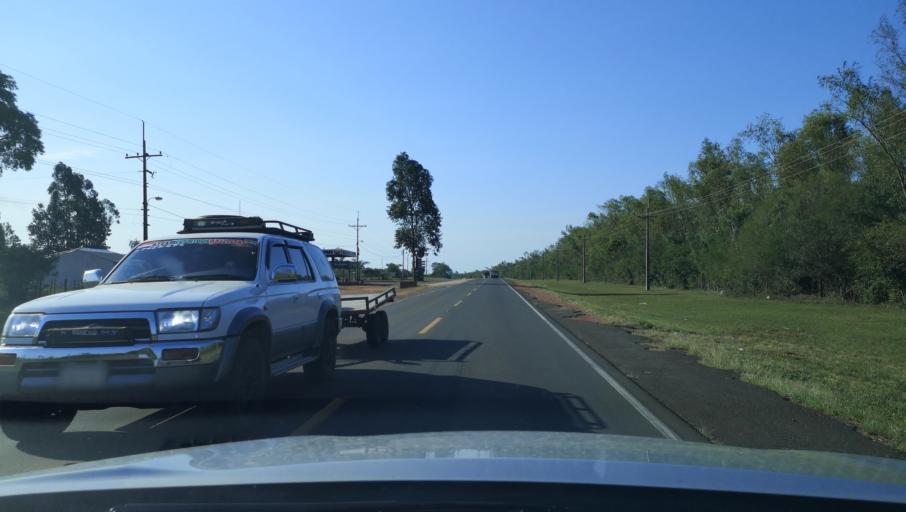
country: PY
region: Misiones
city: Santa Maria
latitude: -26.7649
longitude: -57.0325
